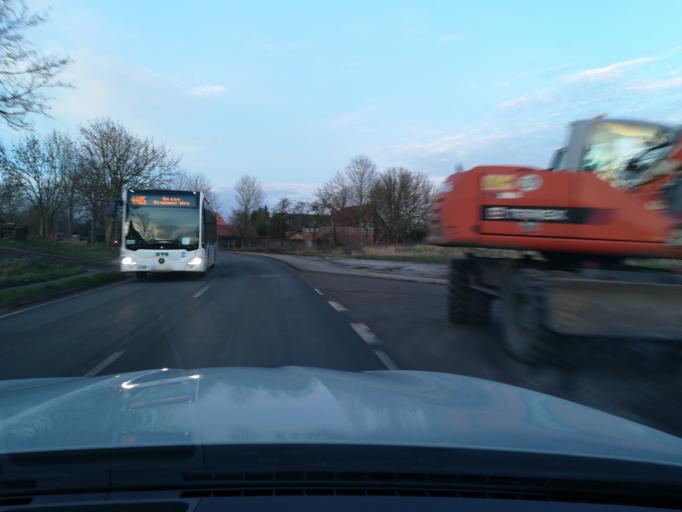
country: DE
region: Lower Saxony
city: Drage
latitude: 53.4096
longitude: 10.2609
